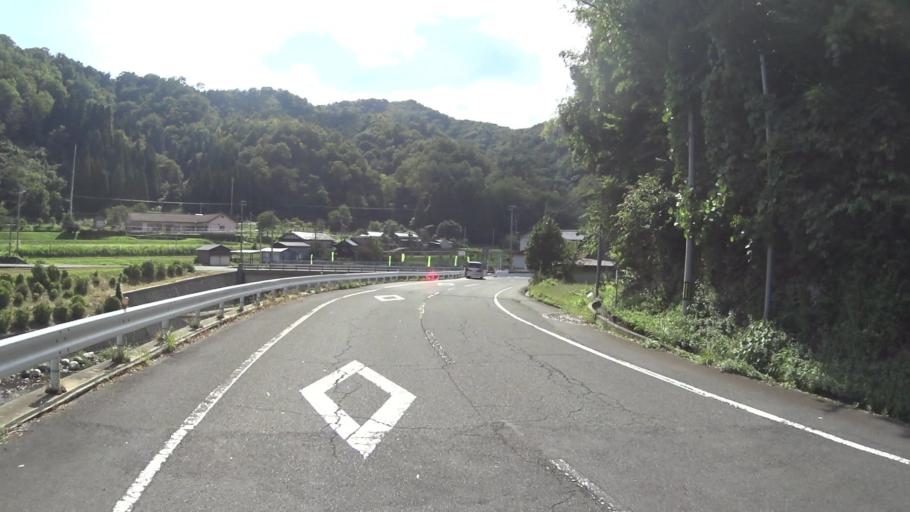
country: JP
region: Kyoto
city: Miyazu
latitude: 35.6849
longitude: 135.1549
